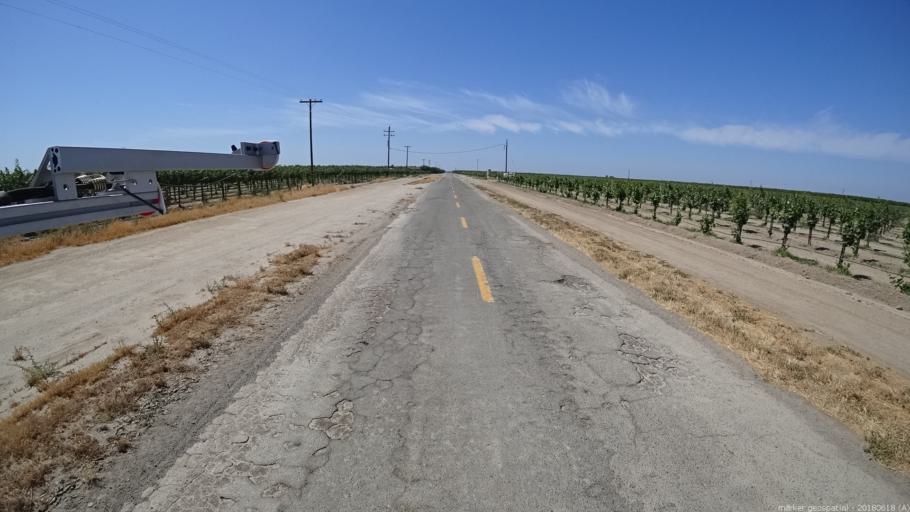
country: US
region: California
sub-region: Madera County
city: Parkwood
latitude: 36.8609
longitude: -120.1829
